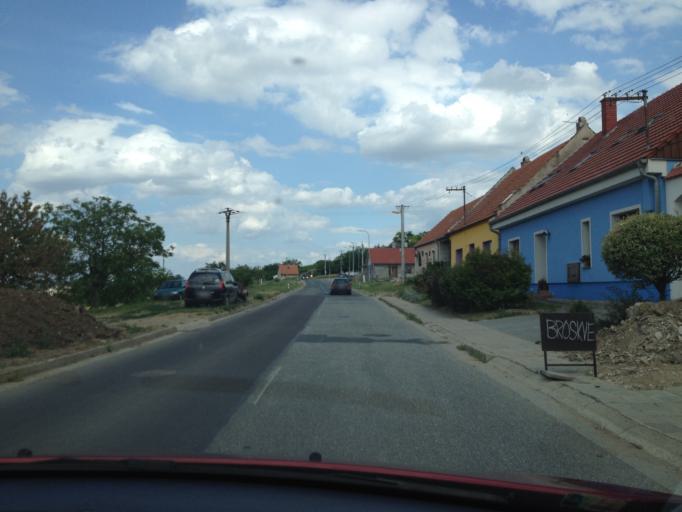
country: CZ
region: South Moravian
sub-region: Okres Breclav
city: Dolni Dunajovice
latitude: 48.8766
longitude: 16.6281
